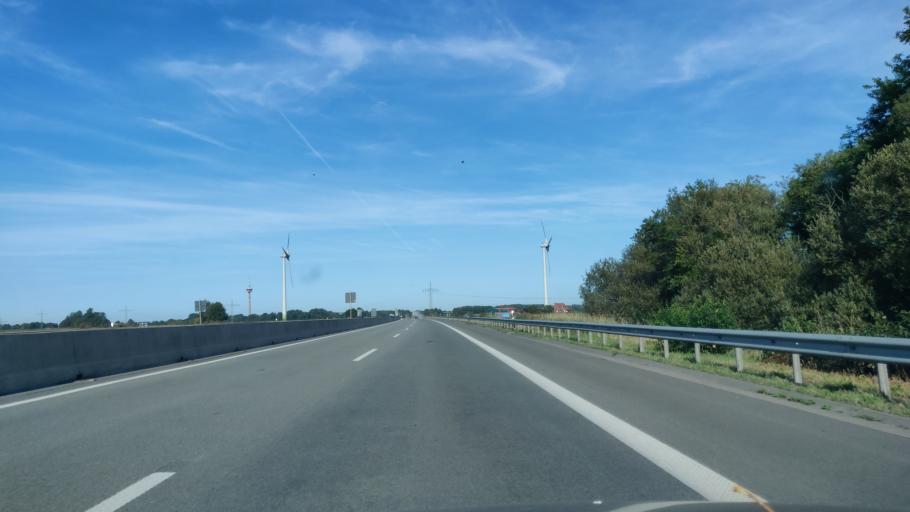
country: DE
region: Lower Saxony
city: Leer
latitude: 53.2440
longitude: 7.4218
